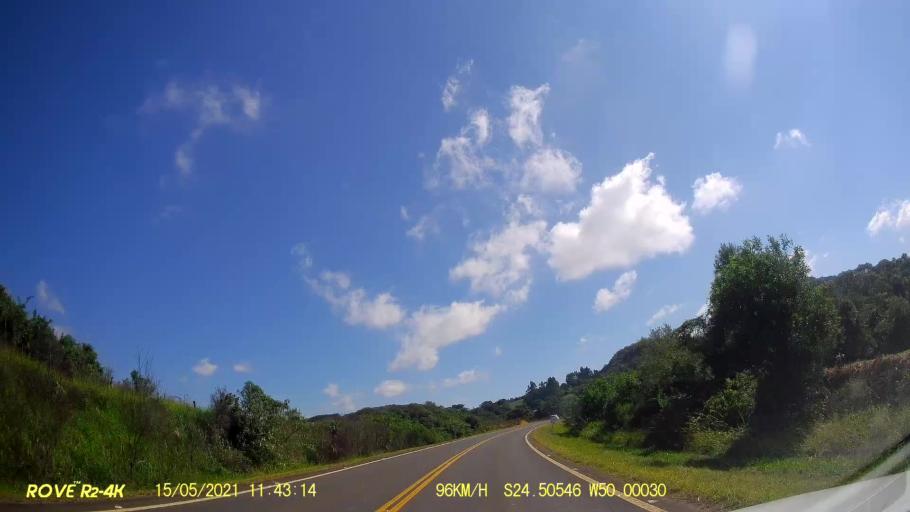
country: BR
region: Parana
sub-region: Pirai Do Sul
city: Pirai do Sul
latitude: -24.5053
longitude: -50.0004
